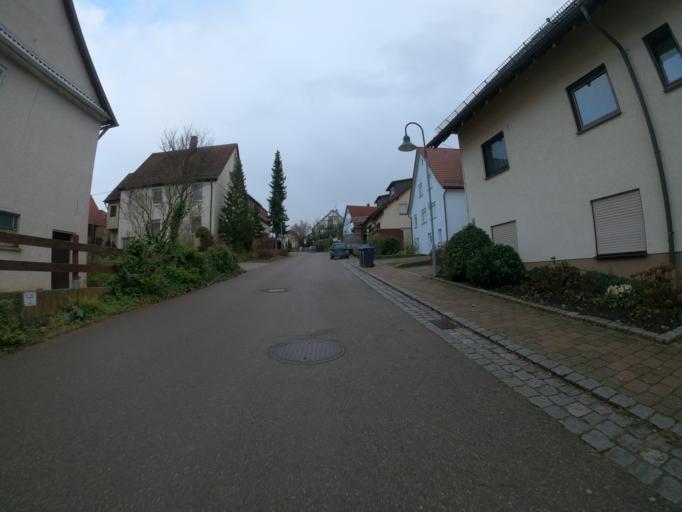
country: DE
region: Baden-Wuerttemberg
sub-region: Regierungsbezirk Stuttgart
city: Waschenbeuren
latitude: 48.7565
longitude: 9.6868
